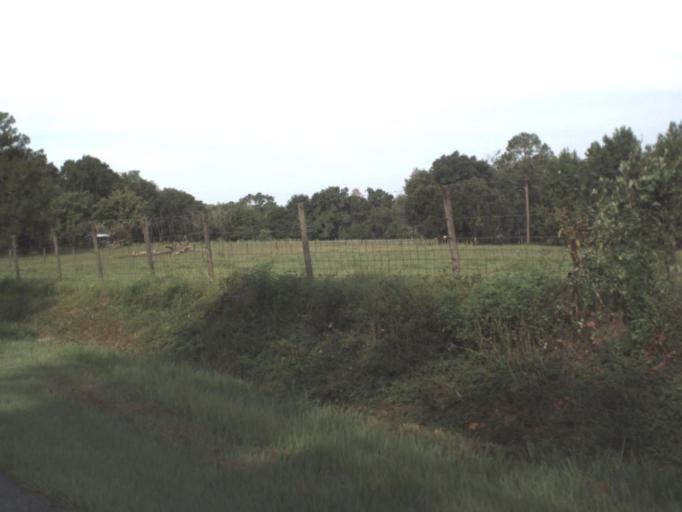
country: US
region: Florida
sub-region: Madison County
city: Madison
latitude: 30.4101
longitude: -83.6421
